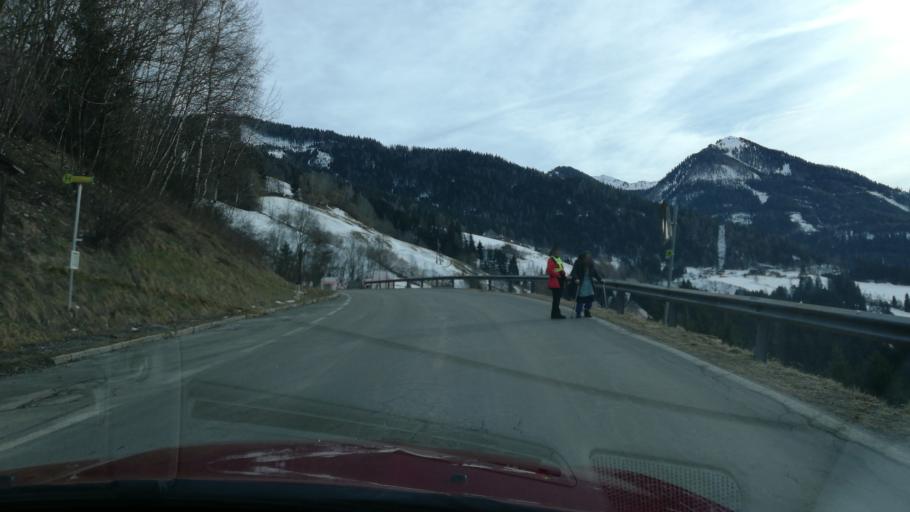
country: AT
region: Styria
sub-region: Politischer Bezirk Liezen
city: Donnersbach
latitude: 47.4559
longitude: 14.1404
